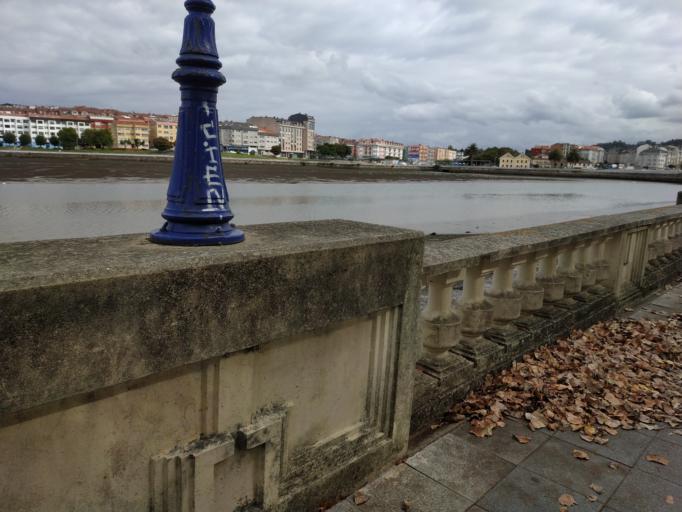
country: ES
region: Galicia
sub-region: Provincia da Coruna
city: Cambre
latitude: 43.3178
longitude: -8.3617
